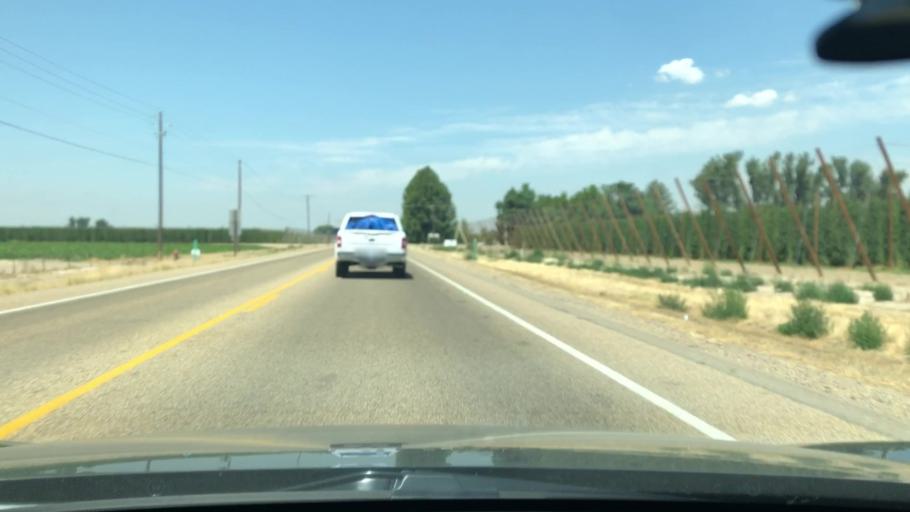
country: US
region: Idaho
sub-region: Canyon County
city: Wilder
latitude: 43.6814
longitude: -116.9120
